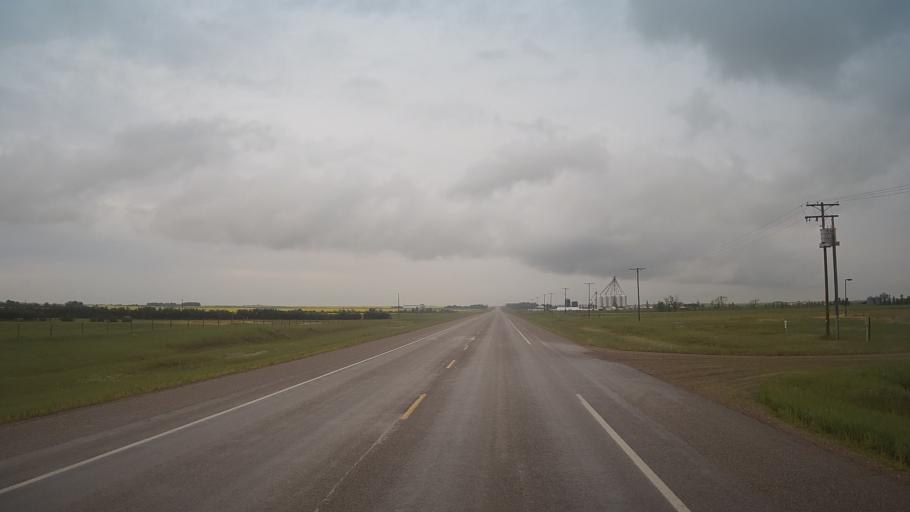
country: CA
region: Saskatchewan
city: Wilkie
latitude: 52.4056
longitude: -108.7467
